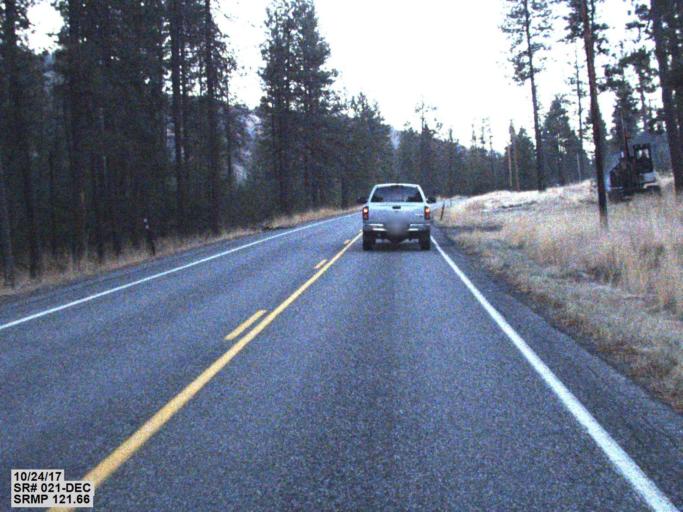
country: US
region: Washington
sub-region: Okanogan County
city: Coulee Dam
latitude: 48.1452
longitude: -118.6934
